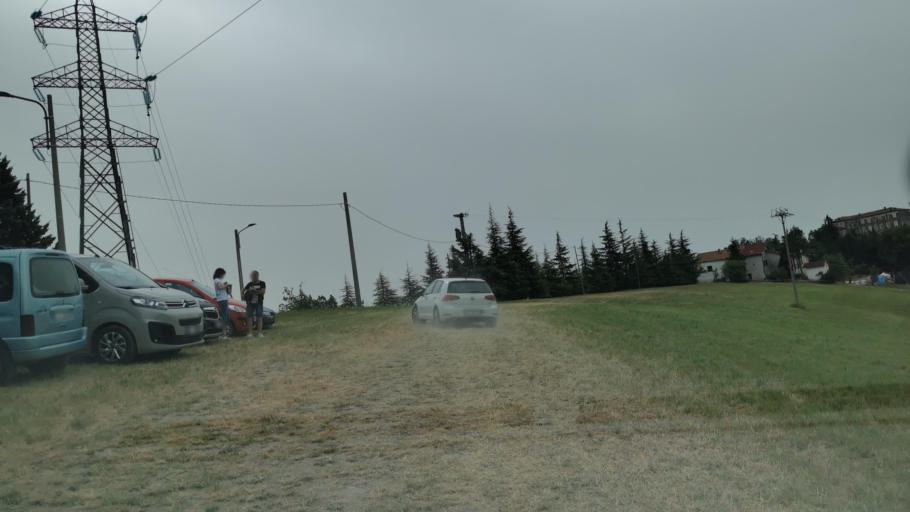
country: IT
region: Piedmont
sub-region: Provincia di Cuneo
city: Sale San Giovanni
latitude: 44.4036
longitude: 8.0758
